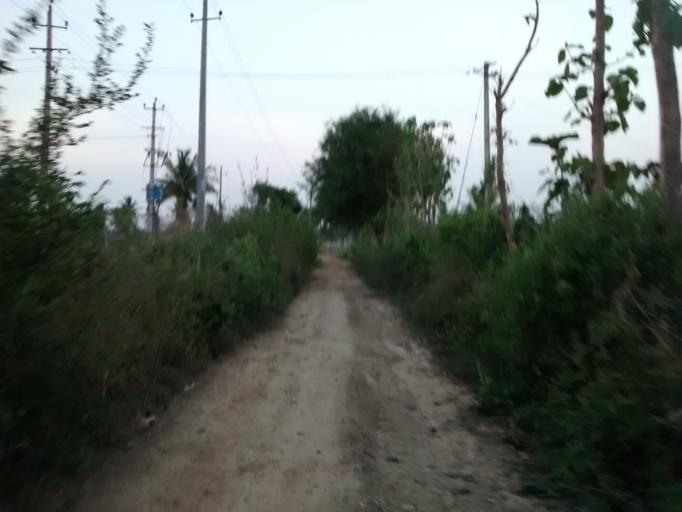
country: IN
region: Karnataka
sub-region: Hassan
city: Hassan
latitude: 12.9384
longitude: 76.1542
